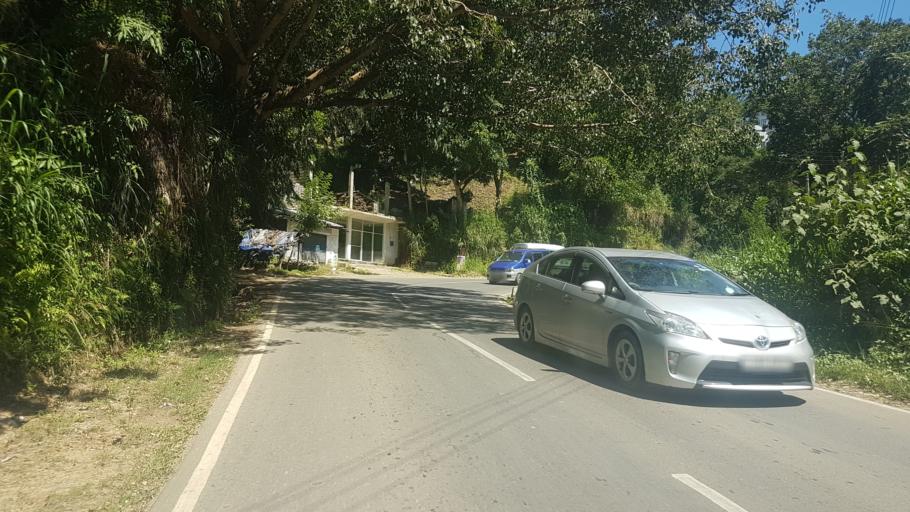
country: LK
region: Uva
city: Badulla
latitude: 6.8690
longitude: 81.0477
